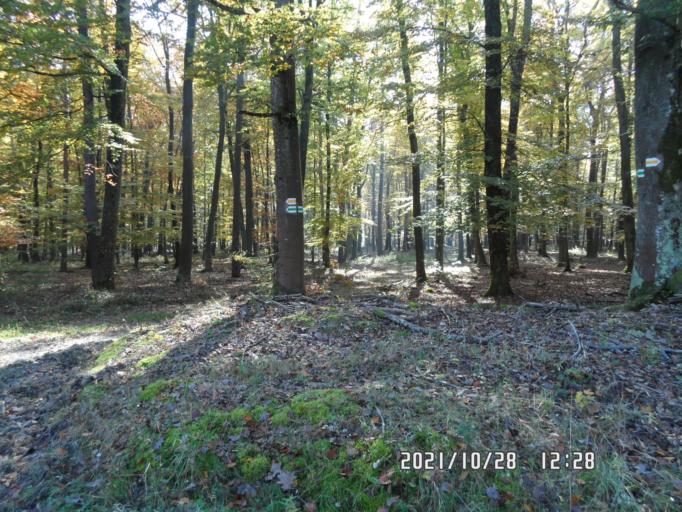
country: SI
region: Hodos-Hodos
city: Hodos
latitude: 46.7805
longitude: 16.3742
